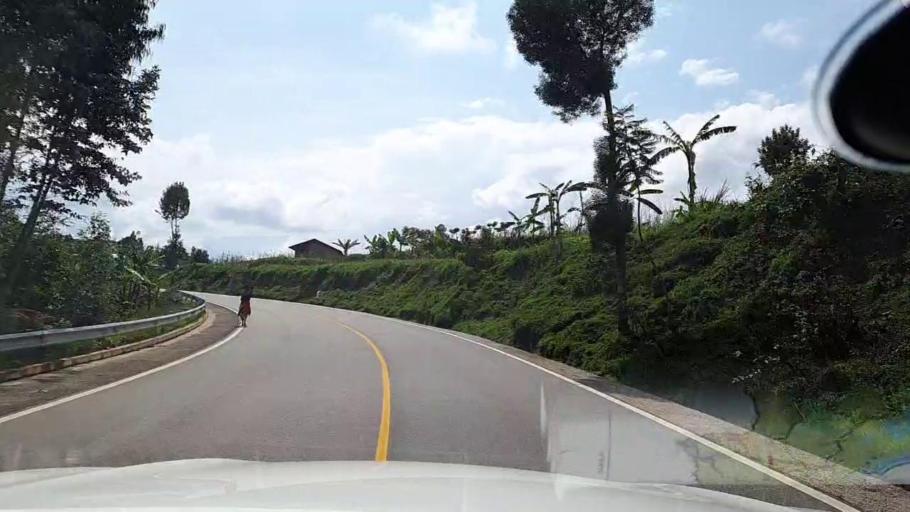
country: RW
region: Southern Province
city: Nzega
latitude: -2.5012
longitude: 29.5087
